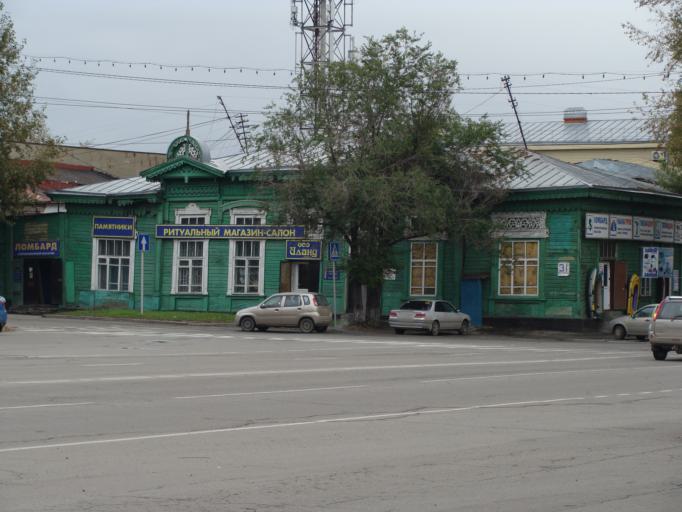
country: RU
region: Altai Krai
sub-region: Gorod Barnaulskiy
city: Barnaul
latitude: 53.3306
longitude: 83.7895
